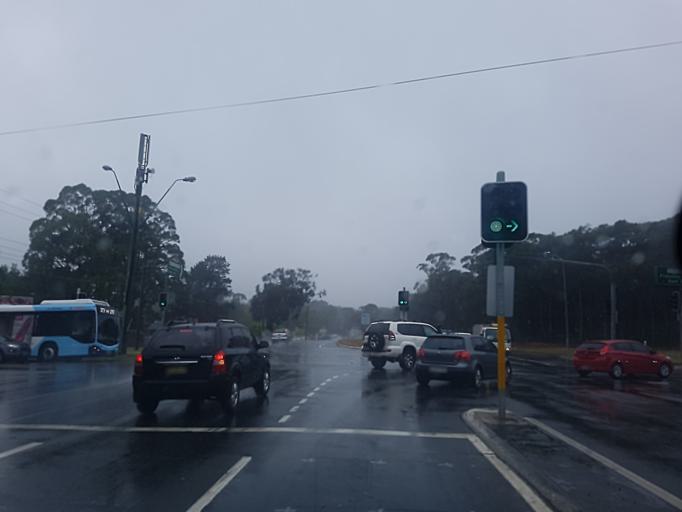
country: AU
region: New South Wales
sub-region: Warringah
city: Davidson
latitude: -33.7009
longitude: 151.2124
